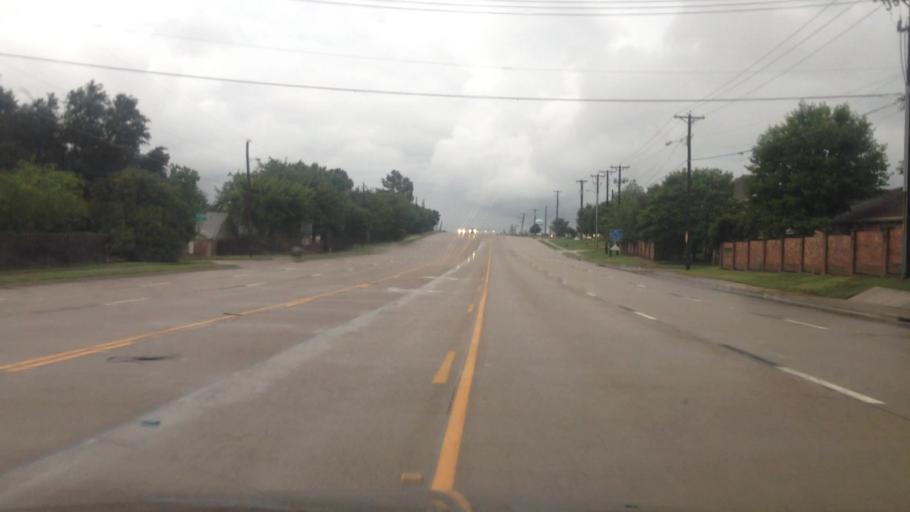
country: US
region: Texas
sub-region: Tarrant County
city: Colleyville
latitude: 32.8691
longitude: -97.1862
